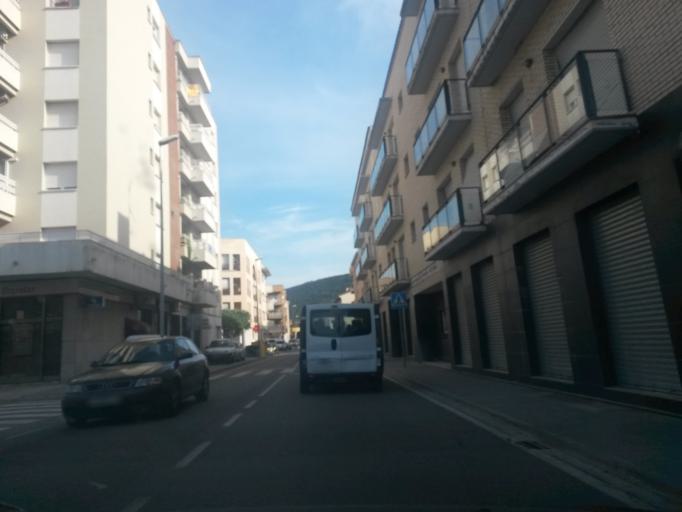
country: ES
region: Catalonia
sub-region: Provincia de Girona
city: la Cellera de Ter
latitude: 42.0079
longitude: 2.6049
